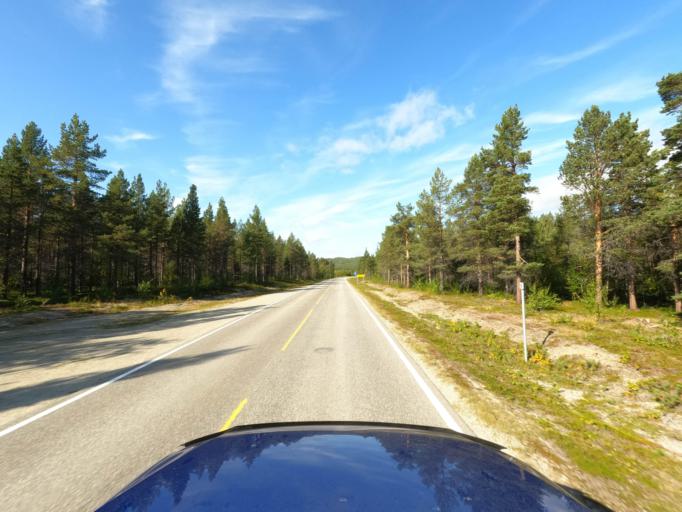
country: NO
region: Finnmark Fylke
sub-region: Porsanger
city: Lakselv
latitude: 69.8237
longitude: 25.1512
